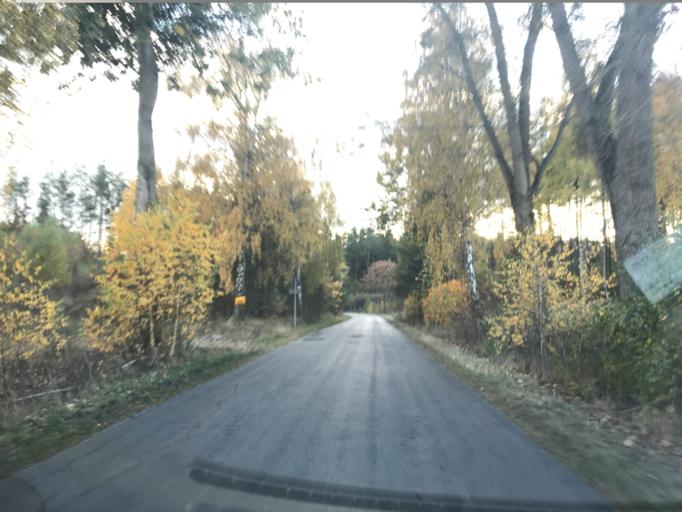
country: PL
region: Warmian-Masurian Voivodeship
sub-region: Powiat dzialdowski
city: Lidzbark
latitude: 53.2372
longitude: 19.7990
